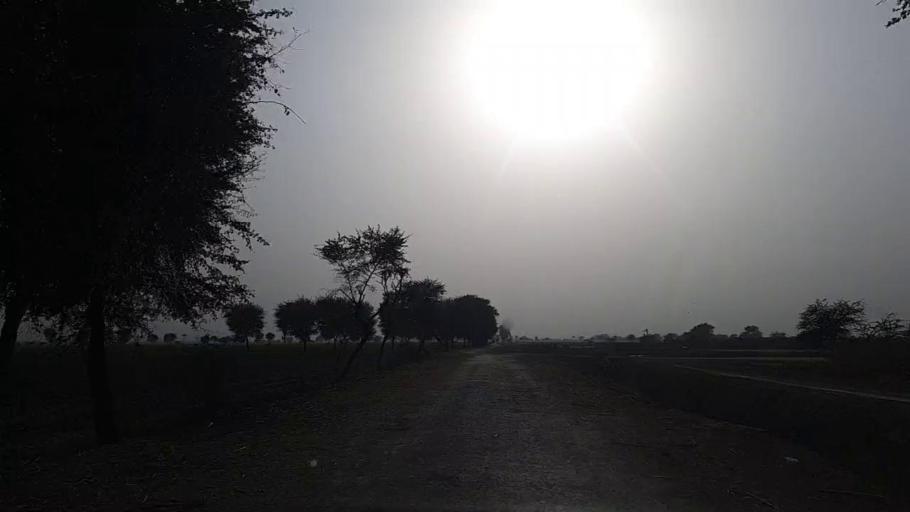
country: PK
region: Sindh
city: Pithoro
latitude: 25.4404
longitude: 69.2922
